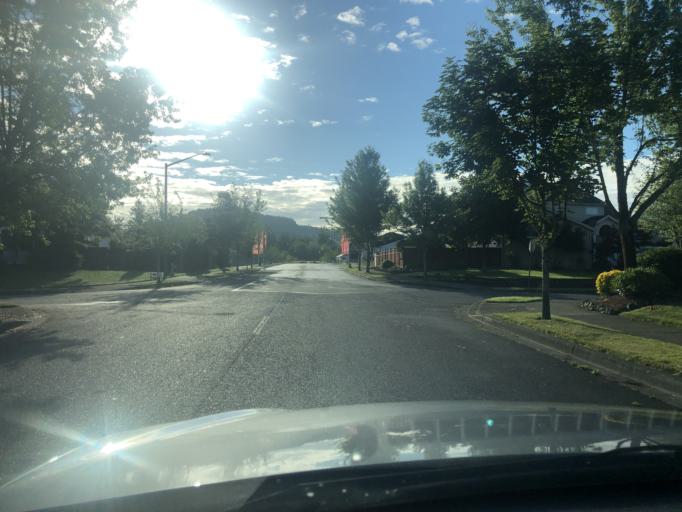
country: US
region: Washington
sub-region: Pierce County
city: Buckley
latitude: 47.1690
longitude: -122.0171
